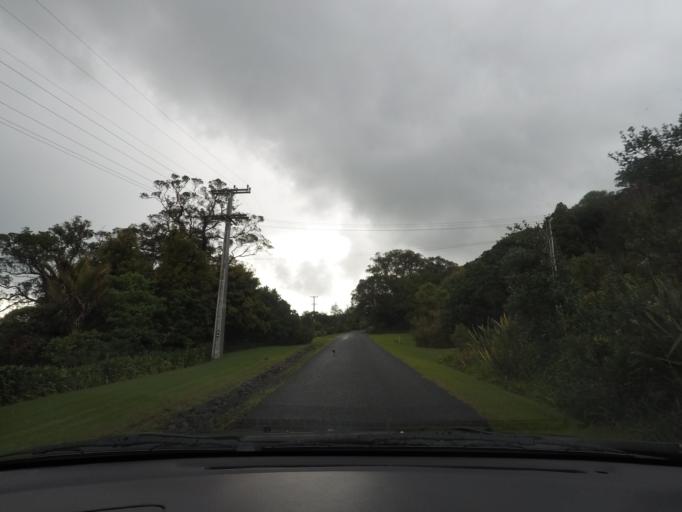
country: NZ
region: Auckland
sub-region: Auckland
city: Warkworth
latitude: -36.4748
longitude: 174.7356
